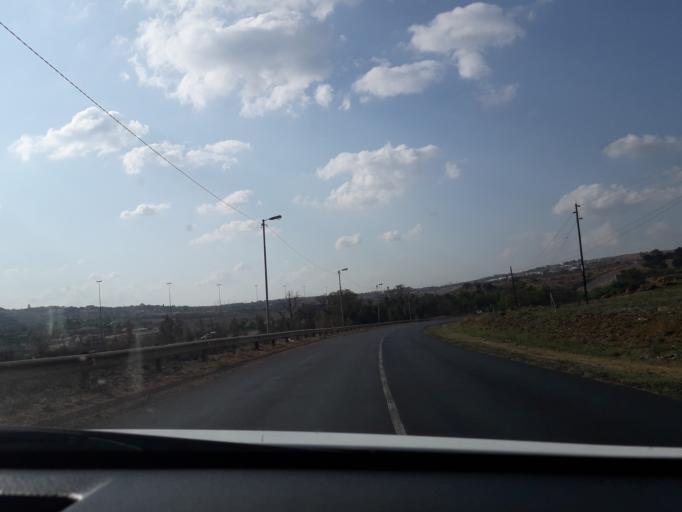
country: ZA
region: Gauteng
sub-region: City of Tshwane Metropolitan Municipality
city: Centurion
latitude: -25.8816
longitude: 28.2560
